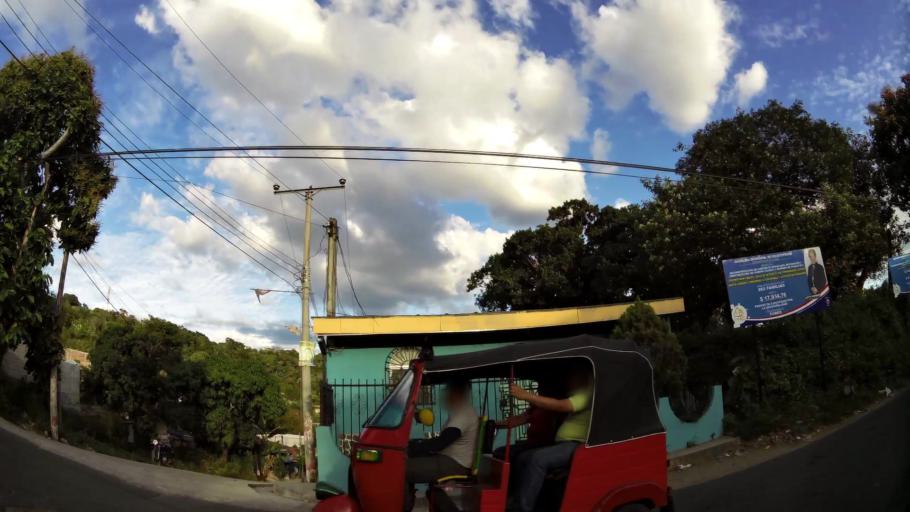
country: SV
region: Cuscatlan
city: Cojutepeque
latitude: 13.7158
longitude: -88.9268
